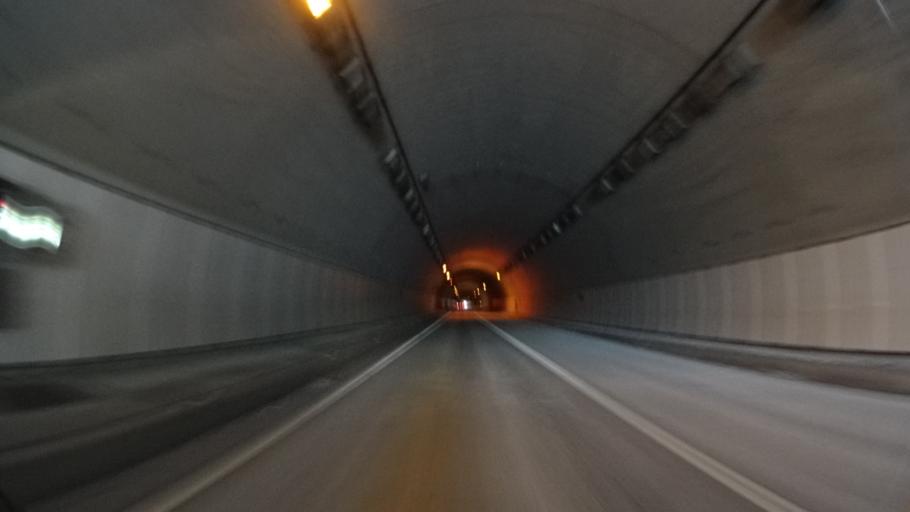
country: JP
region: Ehime
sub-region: Nishiuwa-gun
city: Ikata-cho
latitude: 33.5086
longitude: 132.3962
